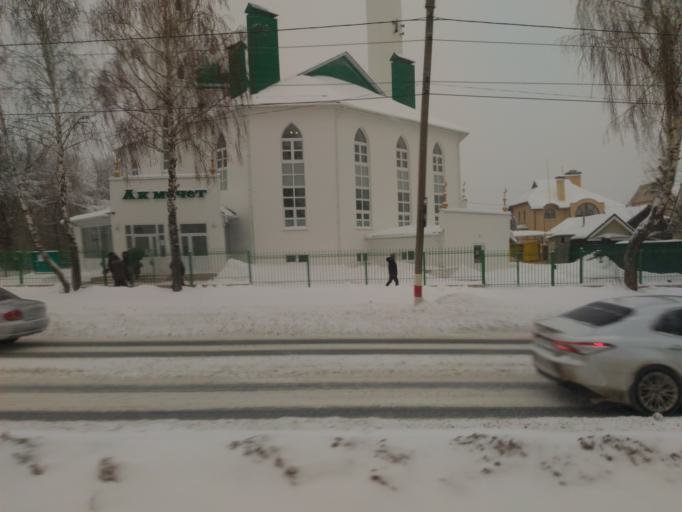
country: RU
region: Ulyanovsk
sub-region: Ulyanovskiy Rayon
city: Ulyanovsk
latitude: 54.3483
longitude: 48.3844
